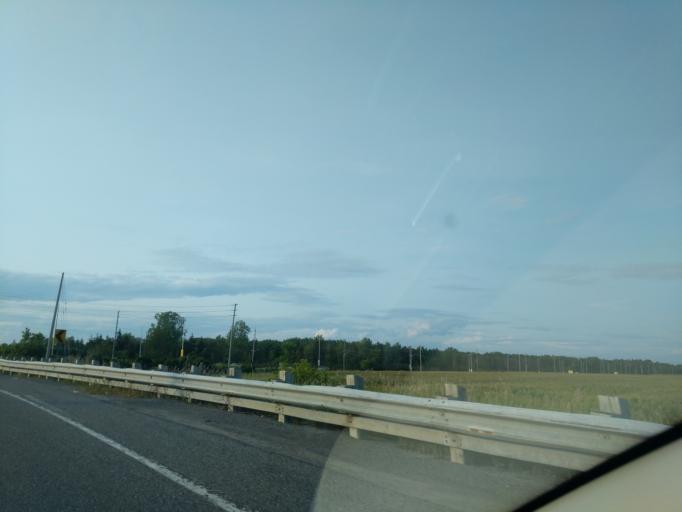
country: CA
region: Ontario
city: Bells Corners
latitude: 45.3128
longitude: -75.7989
